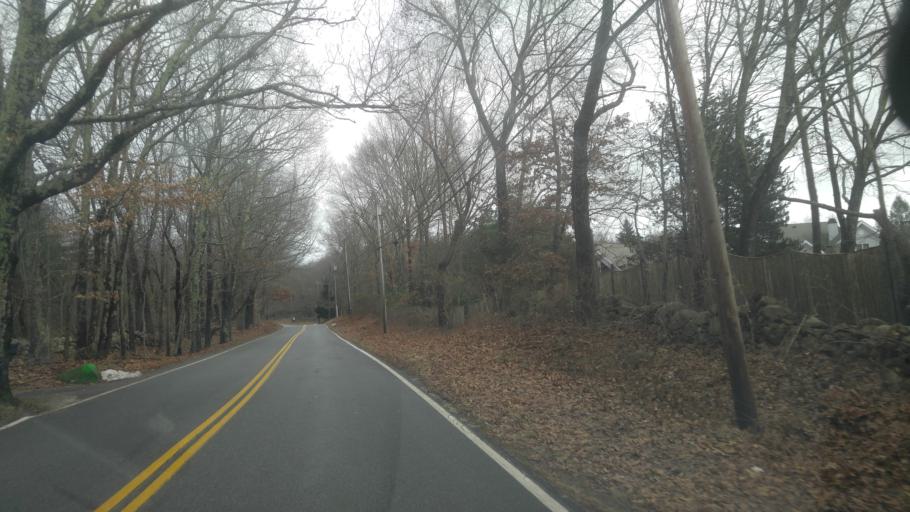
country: US
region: Rhode Island
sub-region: Kent County
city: West Warwick
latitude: 41.6430
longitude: -71.5239
